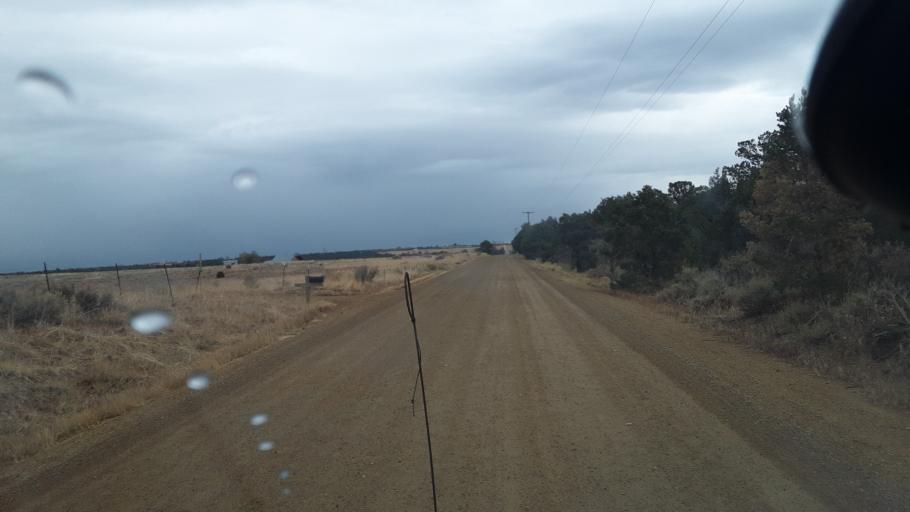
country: US
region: Colorado
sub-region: Montezuma County
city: Mancos
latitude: 37.1984
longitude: -108.1312
